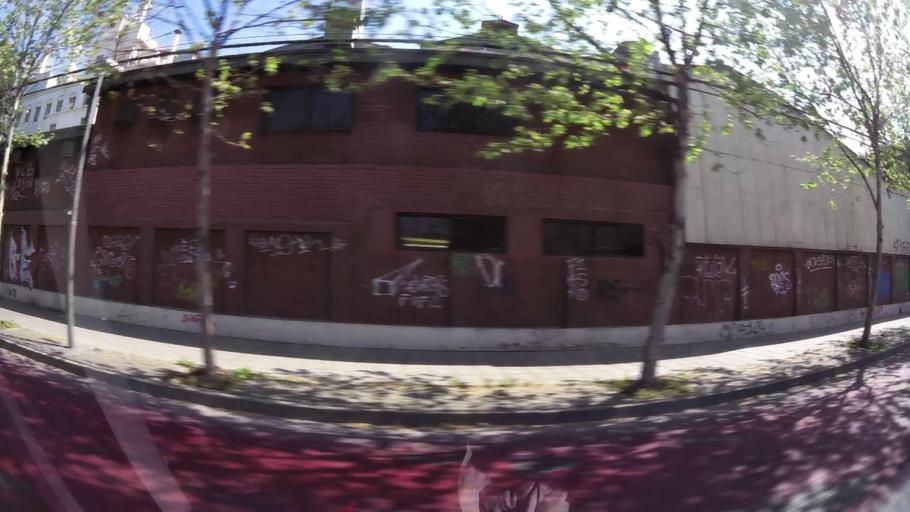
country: CL
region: Santiago Metropolitan
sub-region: Provincia de Santiago
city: Santiago
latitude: -33.4683
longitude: -70.6792
